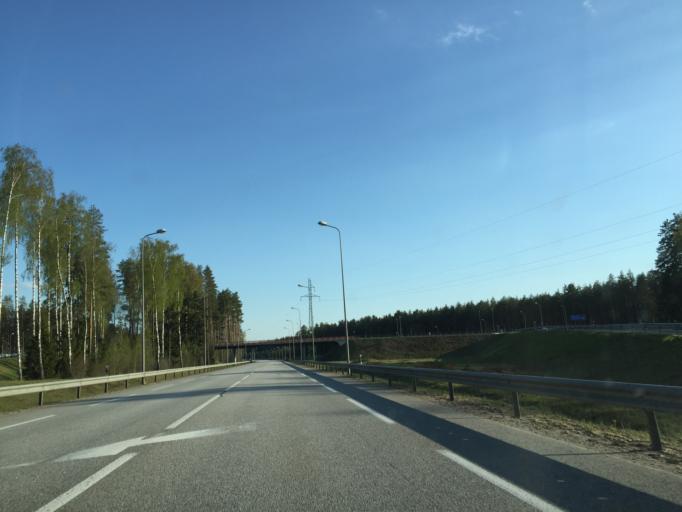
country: LV
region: Saulkrastu
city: Saulkrasti
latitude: 57.2471
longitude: 24.4276
